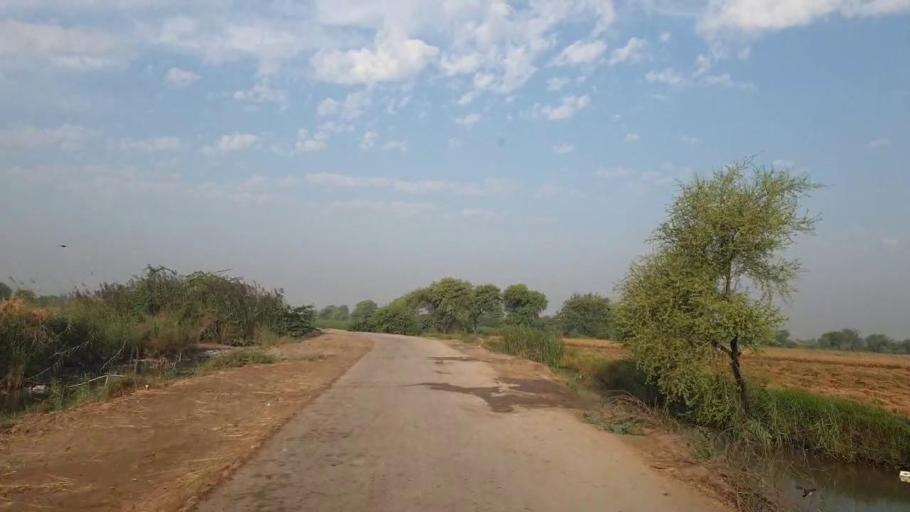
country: PK
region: Sindh
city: Tando Bago
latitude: 24.7955
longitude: 68.9709
